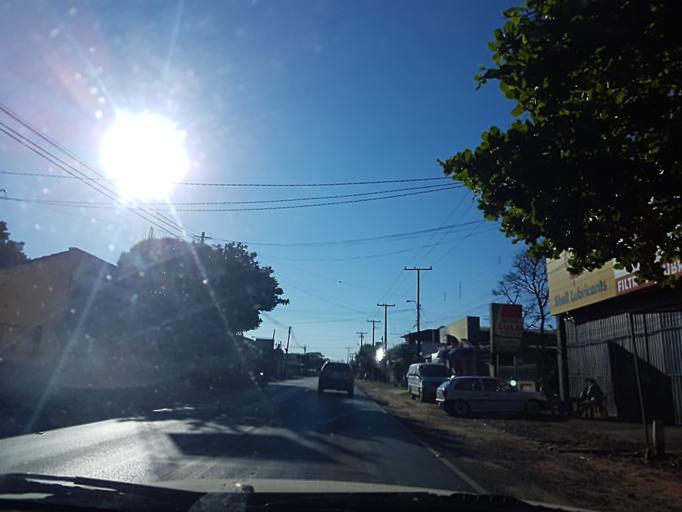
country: PY
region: Central
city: San Lorenzo
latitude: -25.2751
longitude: -57.4799
